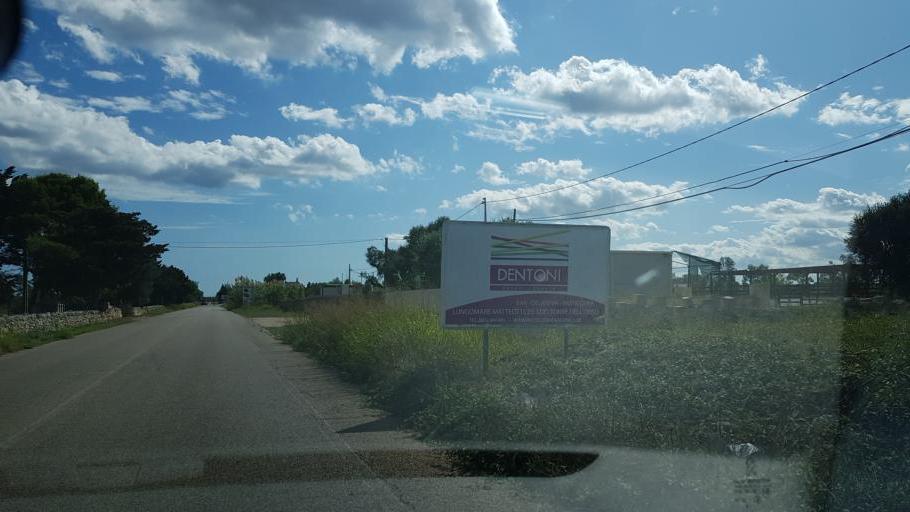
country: IT
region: Apulia
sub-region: Provincia di Lecce
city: Borgagne
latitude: 40.2644
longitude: 18.4325
